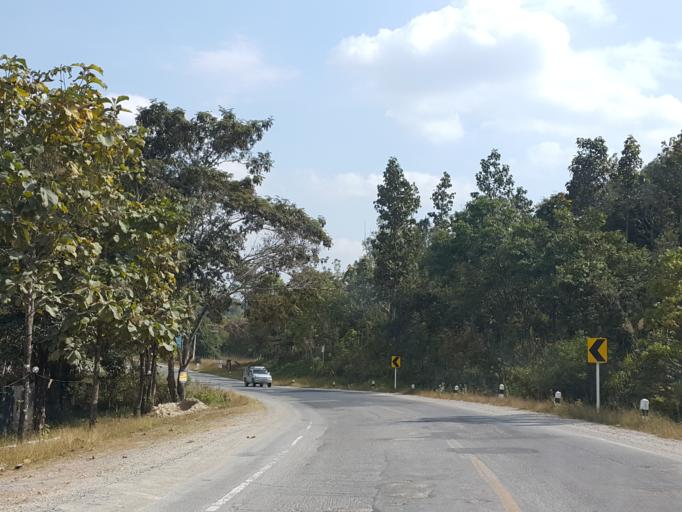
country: TH
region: Chiang Mai
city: Om Koi
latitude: 17.8082
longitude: 98.3631
